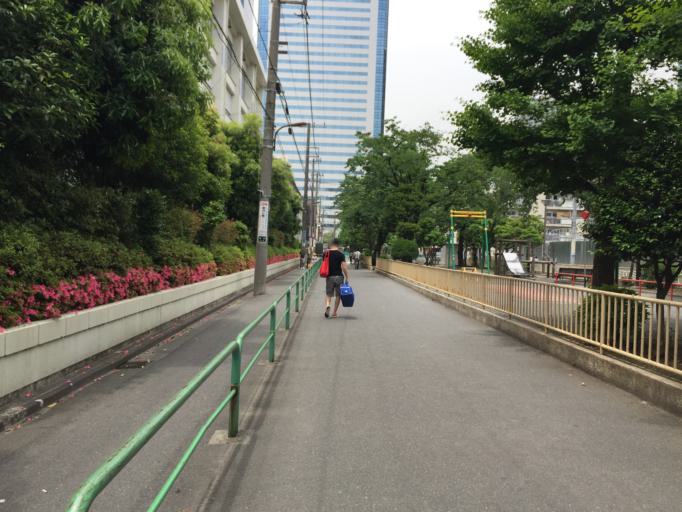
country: JP
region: Tokyo
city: Urayasu
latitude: 35.6539
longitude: 139.7994
